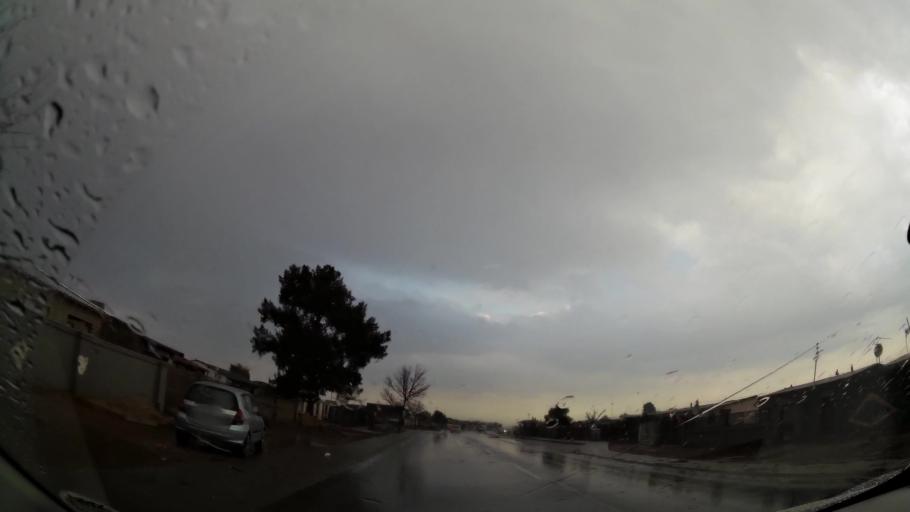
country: ZA
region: Gauteng
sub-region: Ekurhuleni Metropolitan Municipality
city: Germiston
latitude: -26.3515
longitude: 28.1409
